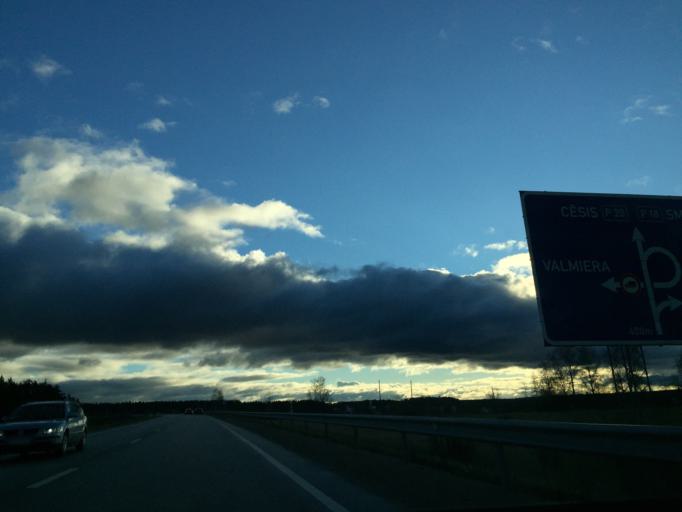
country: LV
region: Koceni
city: Koceni
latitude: 57.5299
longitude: 25.3700
